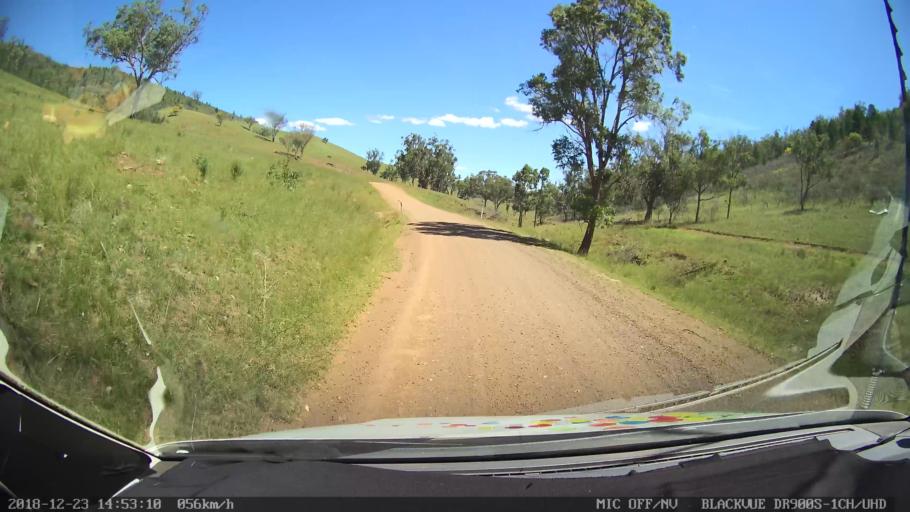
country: AU
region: New South Wales
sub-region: Tamworth Municipality
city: Manilla
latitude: -30.6895
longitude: 150.8519
